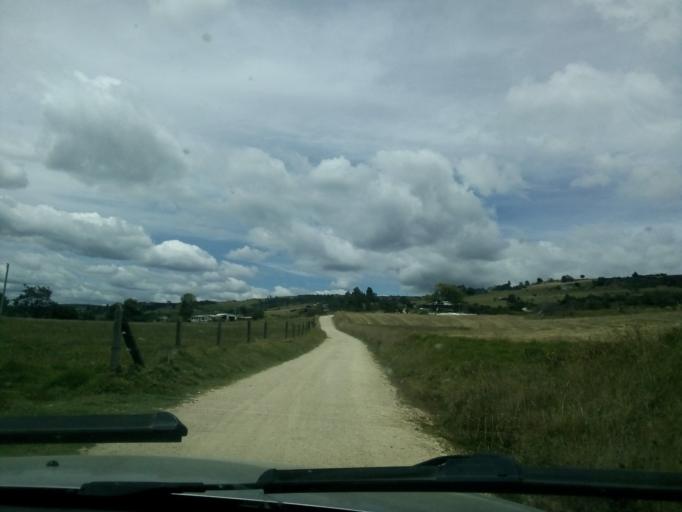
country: CO
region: Boyaca
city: Toca
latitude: 5.6228
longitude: -73.1301
